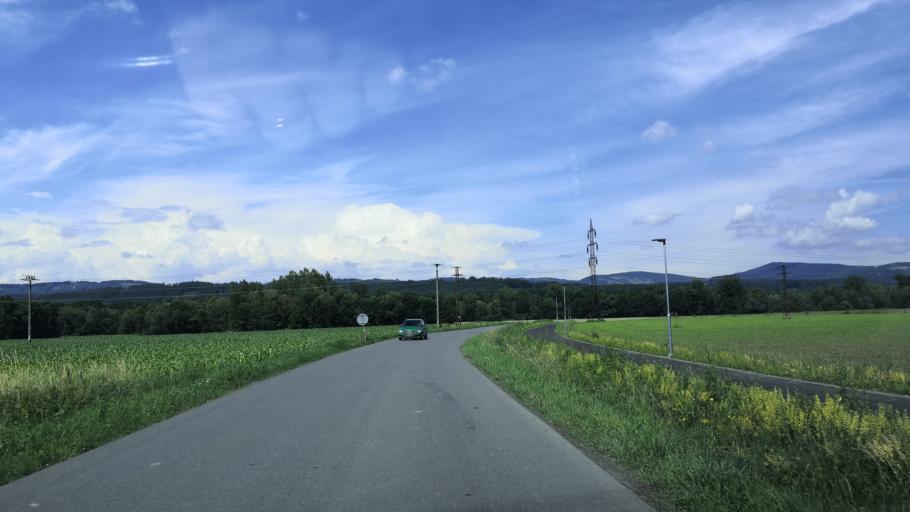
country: CZ
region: Zlin
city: Zasova
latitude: 49.4599
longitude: 18.0563
